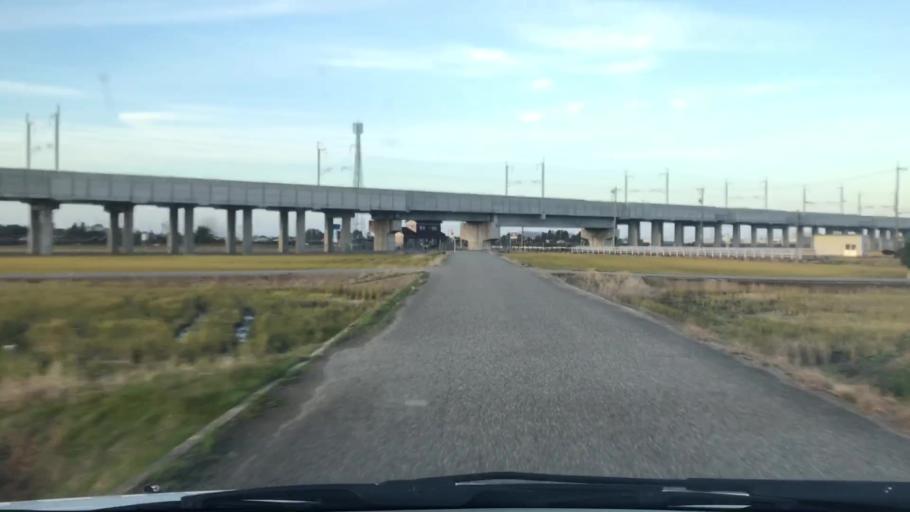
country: JP
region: Toyama
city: Namerikawa
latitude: 36.7307
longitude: 137.3357
